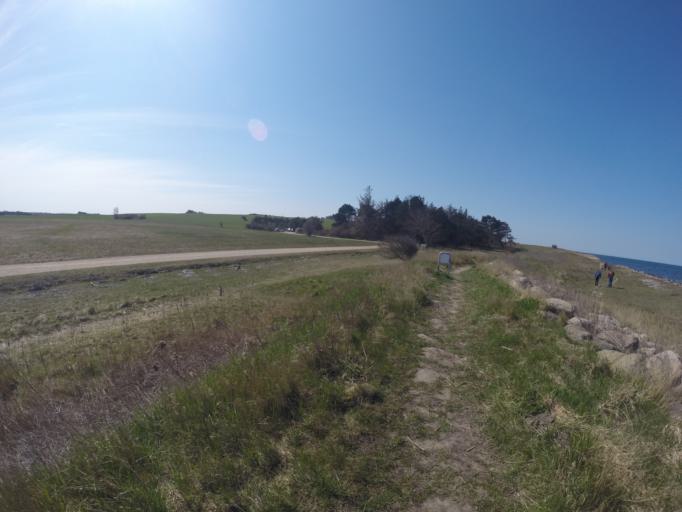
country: DK
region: Zealand
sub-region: Kalundborg Kommune
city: Gorlev
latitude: 55.5344
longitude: 11.0915
